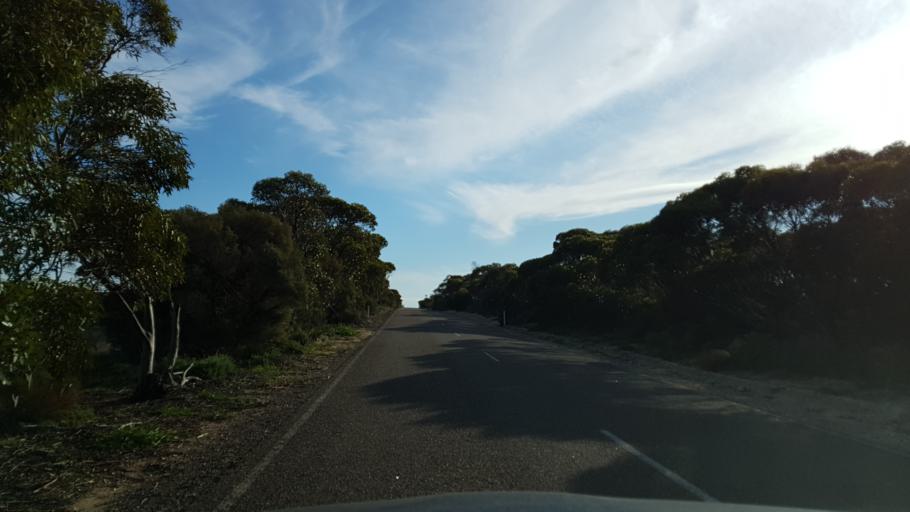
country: AU
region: South Australia
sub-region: Murray Bridge
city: Tailem Bend
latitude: -35.0653
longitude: 139.4651
